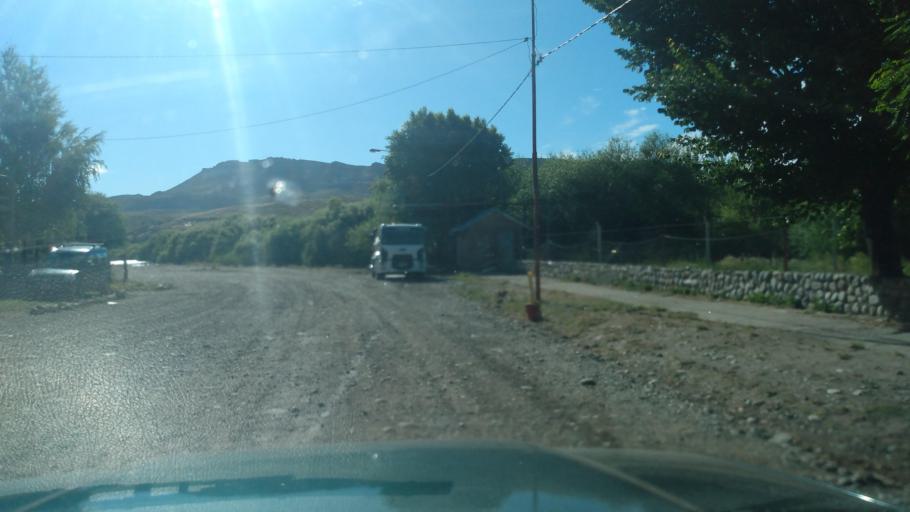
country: AR
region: Neuquen
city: Junin de los Andes
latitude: -39.9586
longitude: -71.0769
